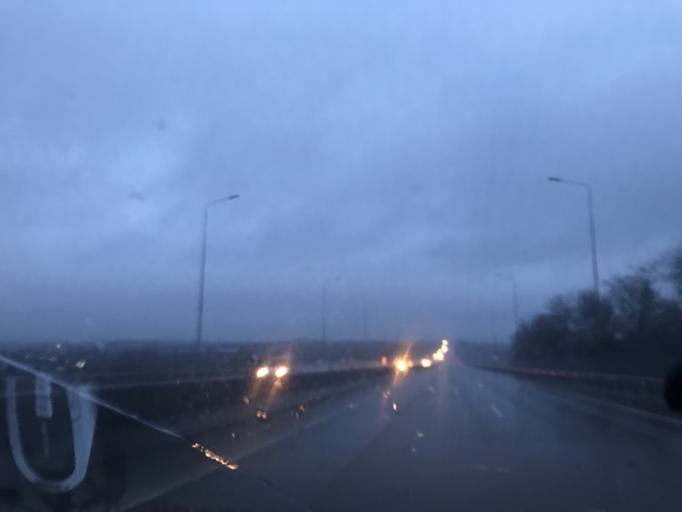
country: RU
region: Rostov
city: Samarskoye
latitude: 46.9926
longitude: 39.7277
